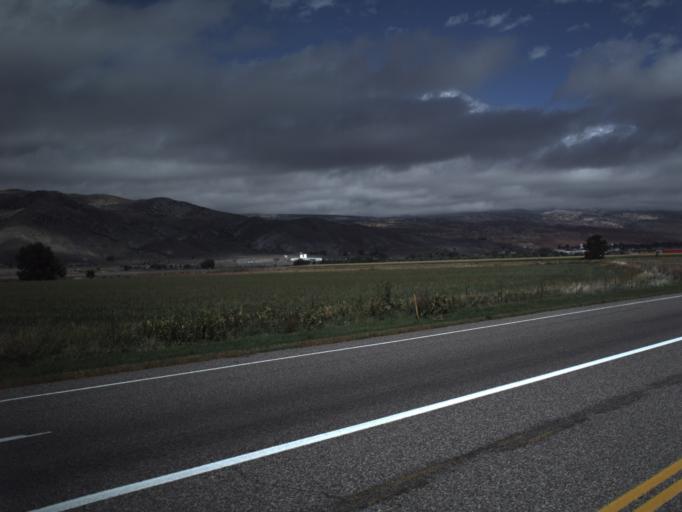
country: US
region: Utah
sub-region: Sevier County
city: Richfield
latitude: 38.7206
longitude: -112.1018
